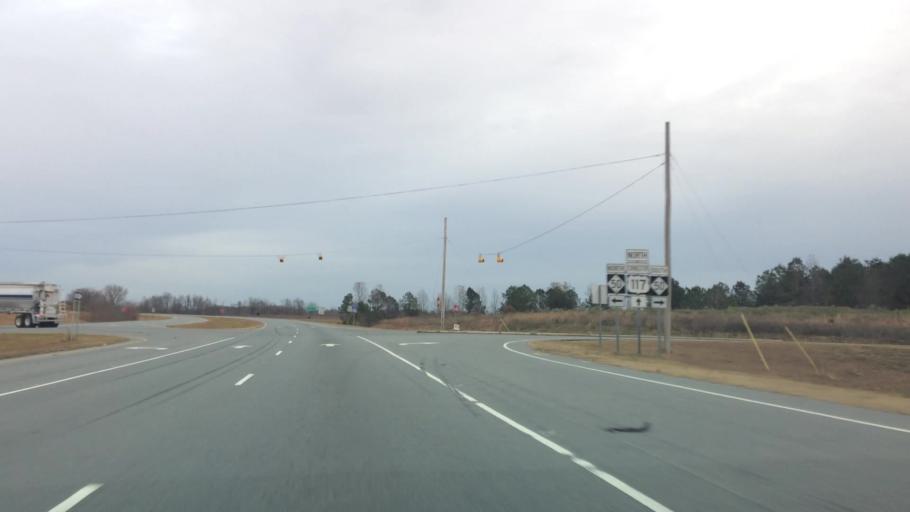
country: US
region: North Carolina
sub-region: Wayne County
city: Mount Olive
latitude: 35.1274
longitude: -78.1530
